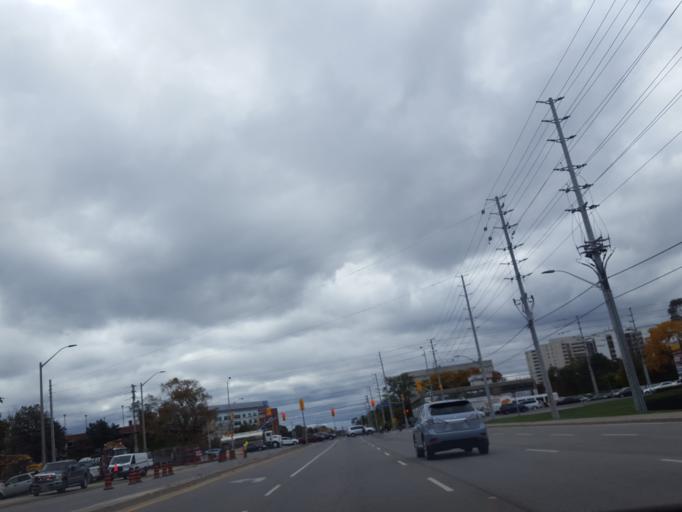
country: CA
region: Ontario
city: Mississauga
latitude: 43.5750
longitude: -79.6067
